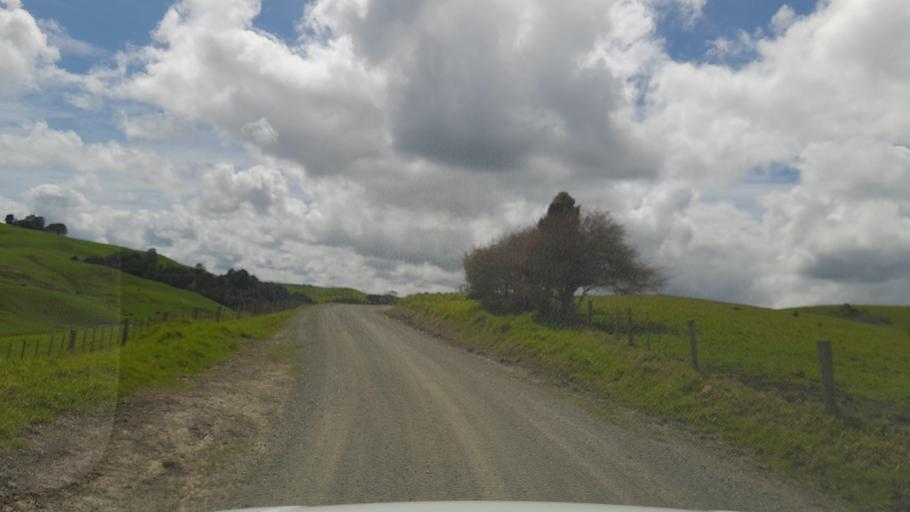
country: NZ
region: Auckland
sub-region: Auckland
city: Wellsford
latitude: -36.2143
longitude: 174.3233
